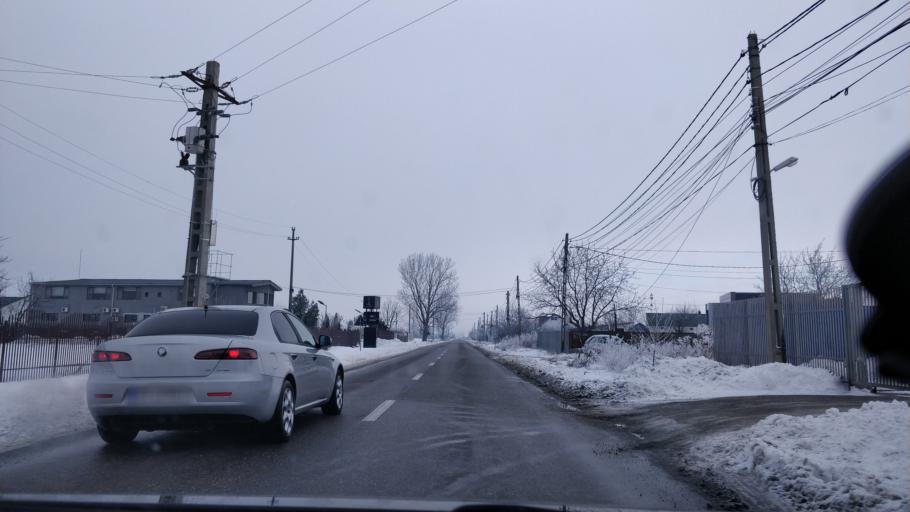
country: RO
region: Vrancea
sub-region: Comuna Vrancioaia
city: Focsani
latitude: 45.6980
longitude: 27.2062
